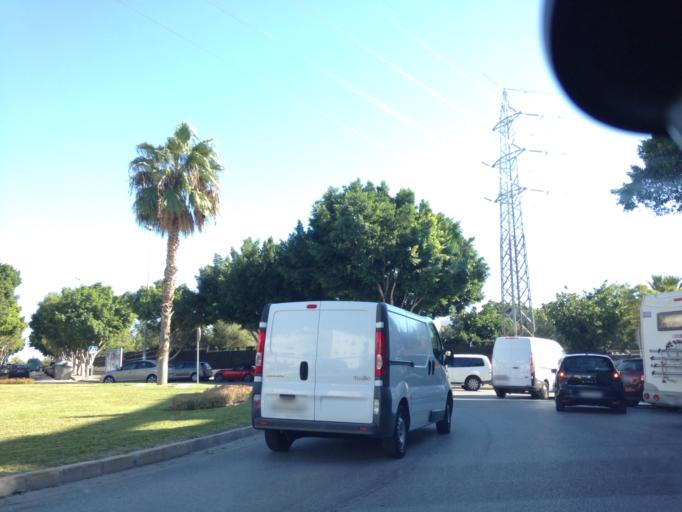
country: ES
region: Andalusia
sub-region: Provincia de Malaga
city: Malaga
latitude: 36.7209
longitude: -4.4750
